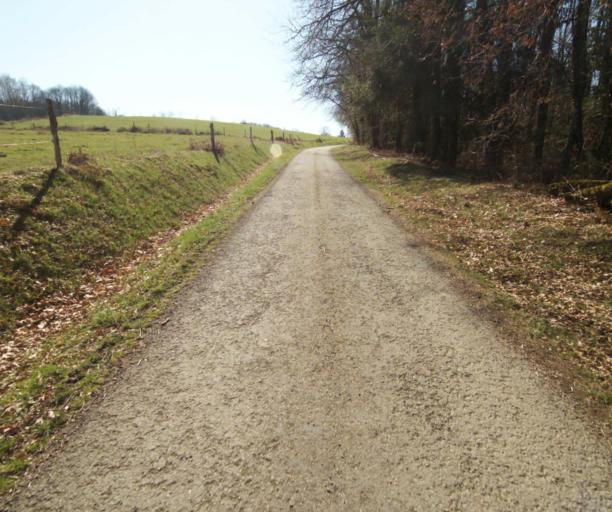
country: FR
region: Limousin
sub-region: Departement de la Correze
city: Saint-Mexant
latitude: 45.3182
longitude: 1.6064
